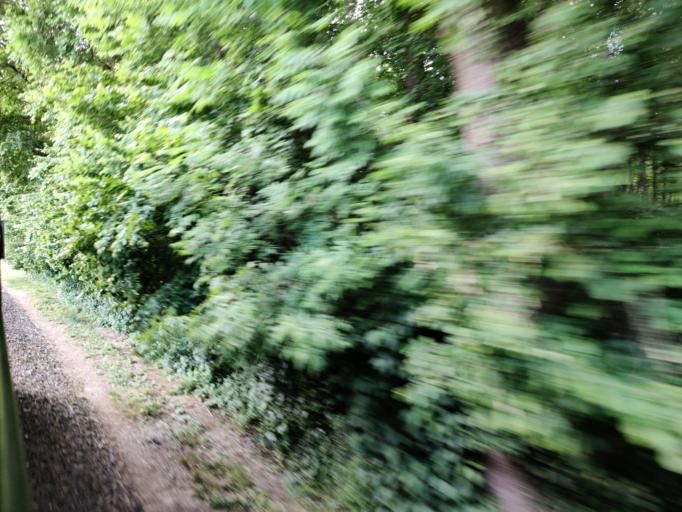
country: AT
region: Styria
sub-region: Politischer Bezirk Suedoststeiermark
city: Eichfeld
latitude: 46.7141
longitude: 15.7417
